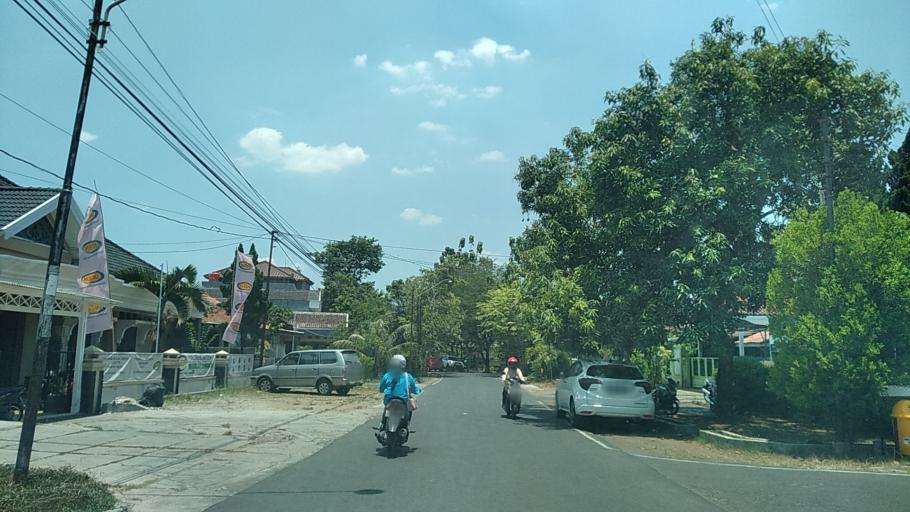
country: ID
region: Central Java
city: Ungaran
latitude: -7.0727
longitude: 110.4250
